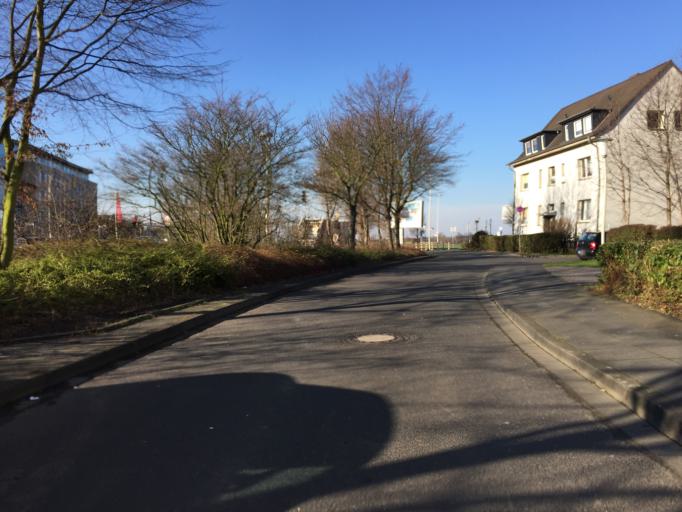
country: DE
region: North Rhine-Westphalia
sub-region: Regierungsbezirk Koln
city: Bonn
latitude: 50.7214
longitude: 7.0632
